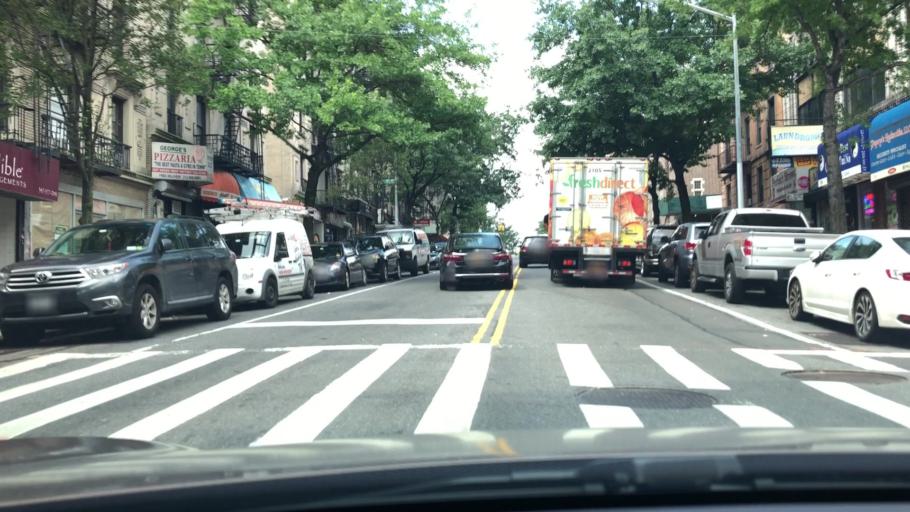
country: US
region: New York
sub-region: New York County
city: Inwood
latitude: 40.8504
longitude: -73.9367
